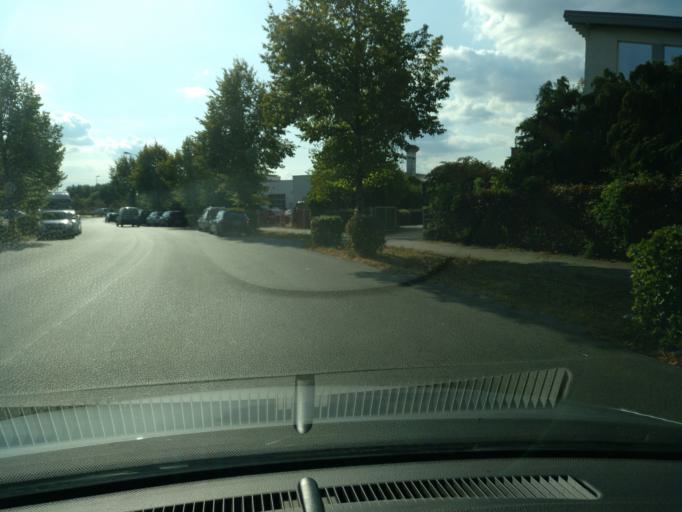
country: DE
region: Berlin
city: Mahlsdorf
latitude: 52.5058
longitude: 13.6342
